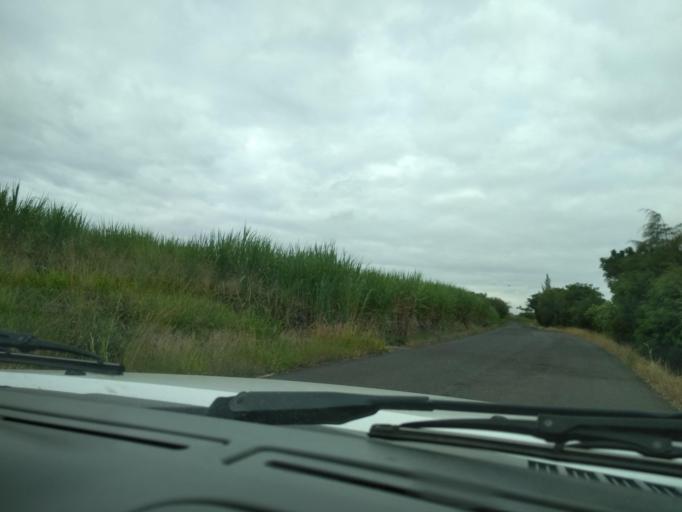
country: MX
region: Veracruz
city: El Castillo
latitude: 19.5845
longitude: -96.8136
